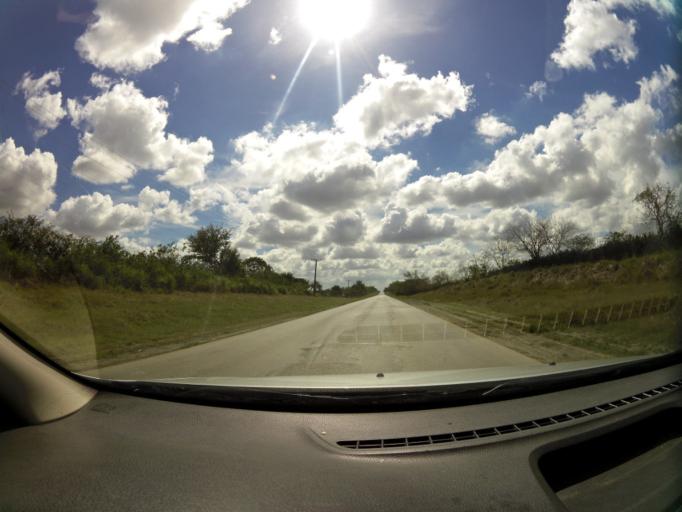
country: CU
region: Las Tunas
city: Las Tunas
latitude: 20.8608
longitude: -76.9117
